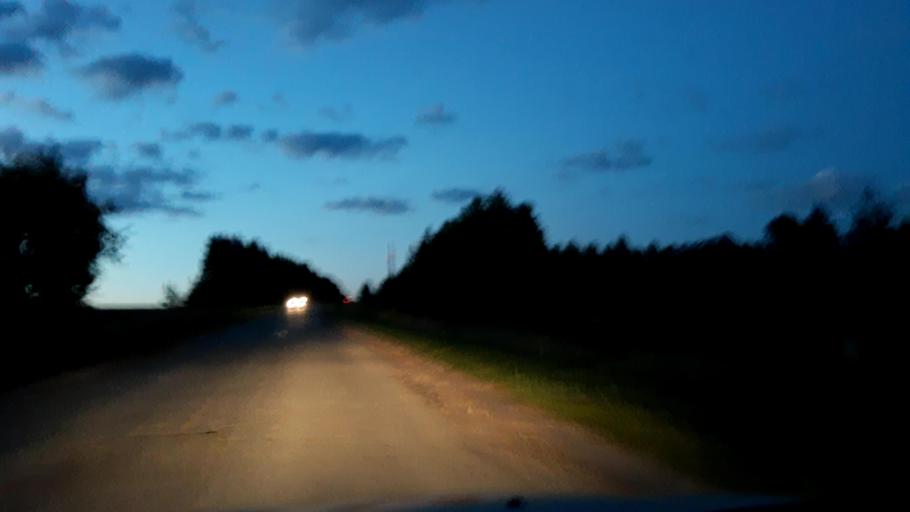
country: RU
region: Nizjnij Novgorod
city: Pamyat' Parizhskoy Kommuny
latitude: 56.0500
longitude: 44.4393
